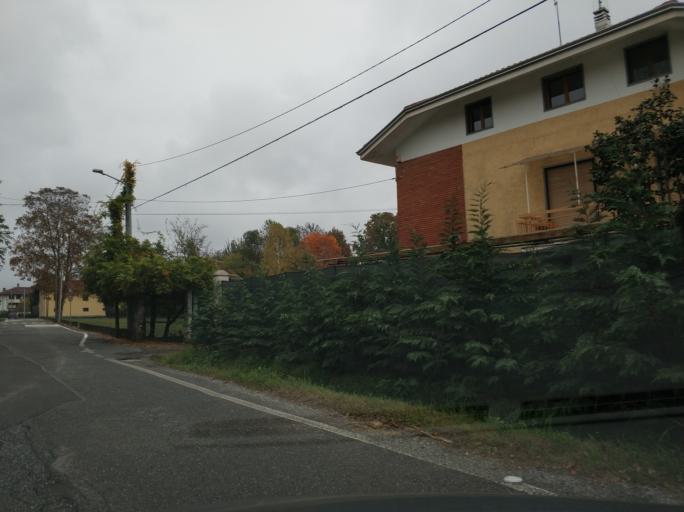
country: IT
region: Piedmont
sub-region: Provincia di Torino
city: Villanova Canavese
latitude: 45.2398
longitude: 7.5559
